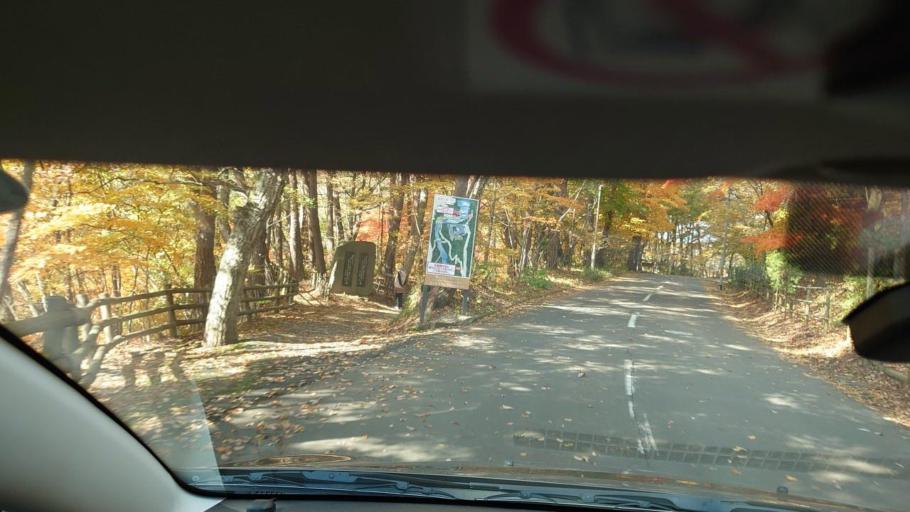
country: JP
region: Iwate
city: Hanamaki
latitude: 39.4538
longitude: 141.0682
